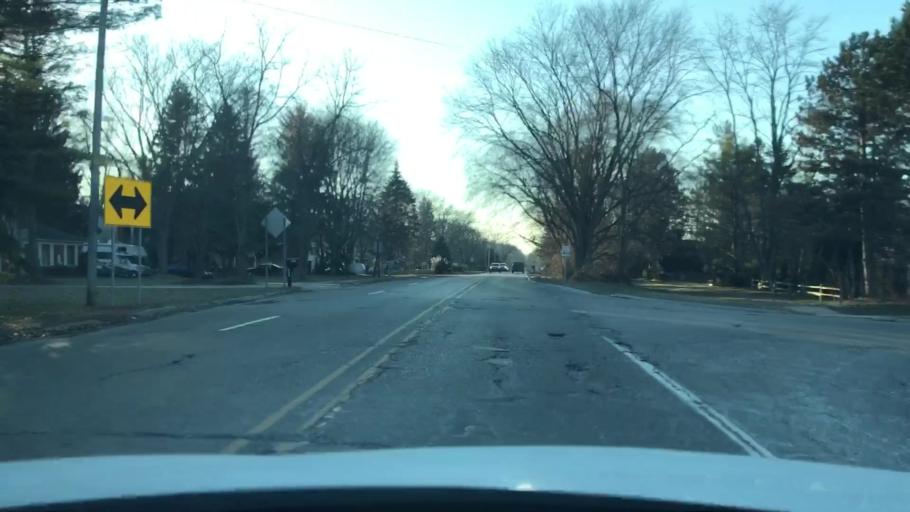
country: US
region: Michigan
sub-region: Oakland County
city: West Bloomfield Township
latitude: 42.5997
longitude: -83.4125
